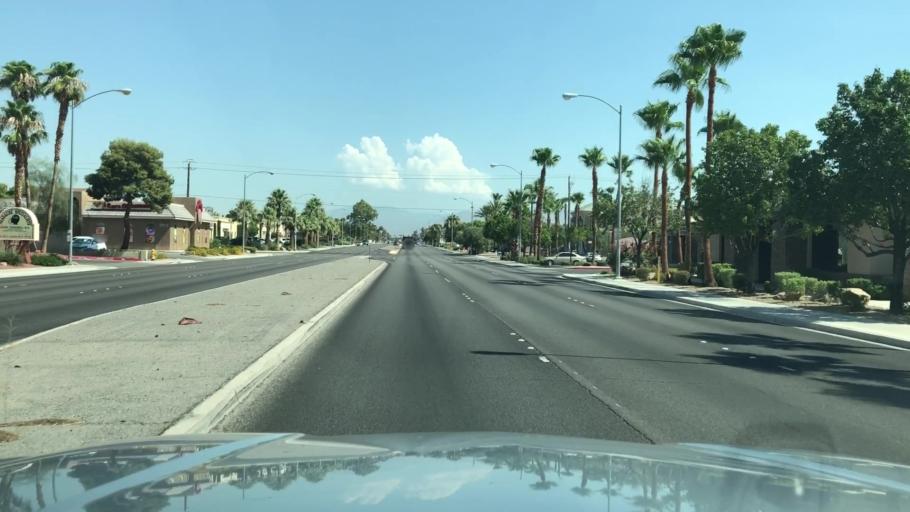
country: US
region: Nevada
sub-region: Clark County
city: Spring Valley
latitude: 36.1375
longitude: -115.2251
